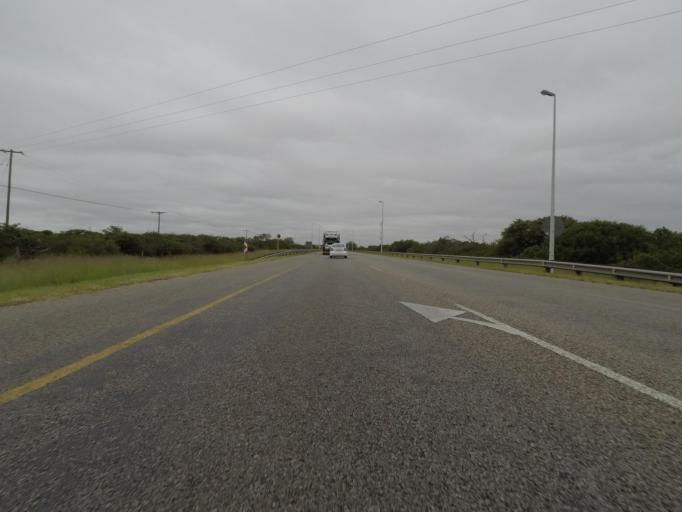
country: ZA
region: Eastern Cape
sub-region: Nelson Mandela Bay Metropolitan Municipality
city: Port Elizabeth
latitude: -33.6496
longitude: 25.8728
